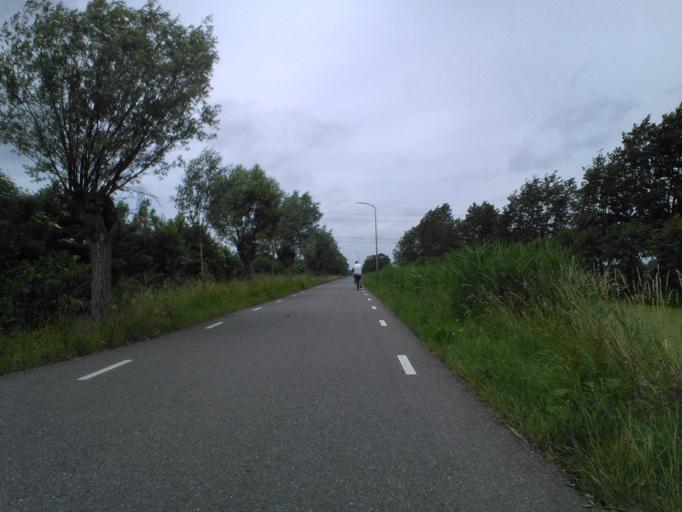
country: NL
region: South Holland
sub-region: Gemeente Vlist
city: Haastrecht
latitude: 51.9940
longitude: 4.7446
